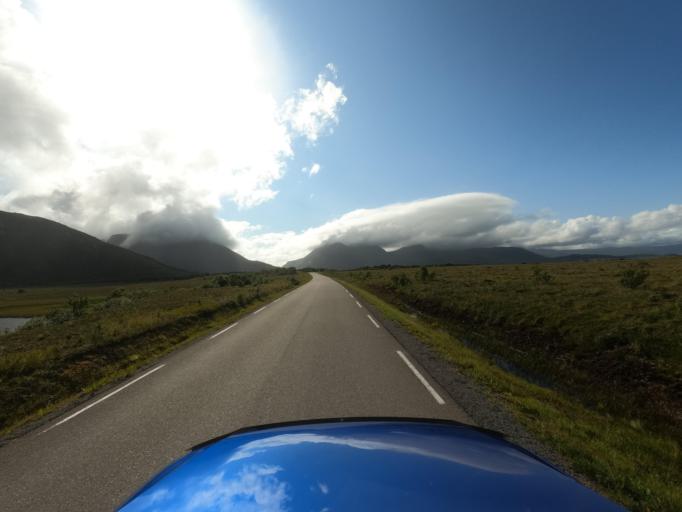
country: NO
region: Nordland
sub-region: Vagan
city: Kabelvag
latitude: 68.3048
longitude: 14.1691
